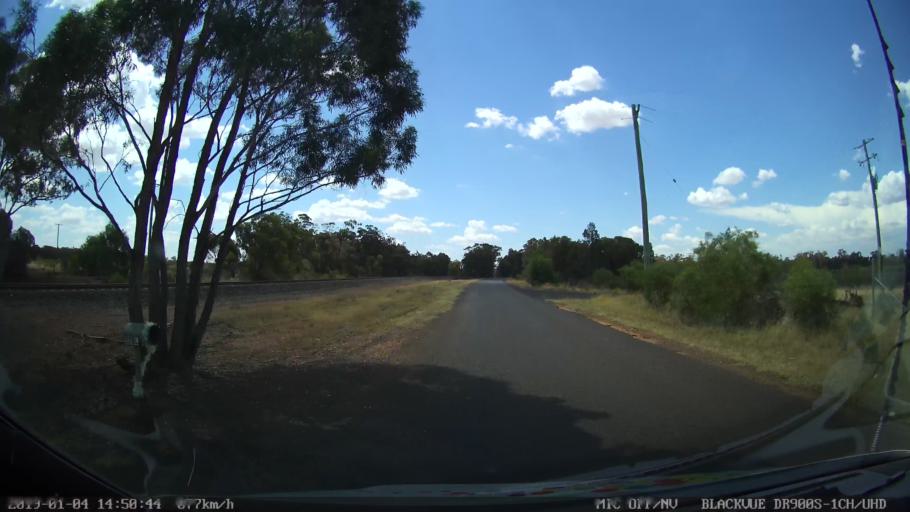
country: AU
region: New South Wales
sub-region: Dubbo Municipality
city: Dubbo
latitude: -32.0346
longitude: 148.6557
